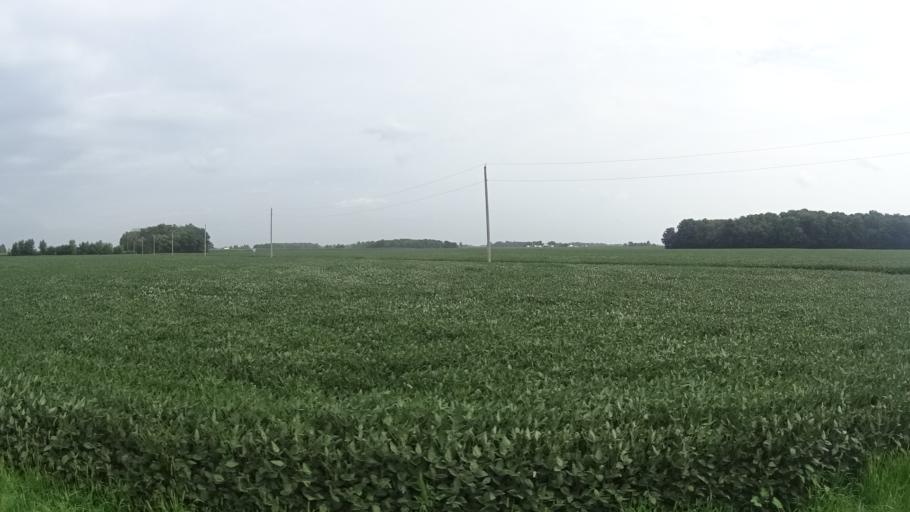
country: US
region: Indiana
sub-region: Madison County
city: Pendleton
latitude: 40.0304
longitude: -85.7874
